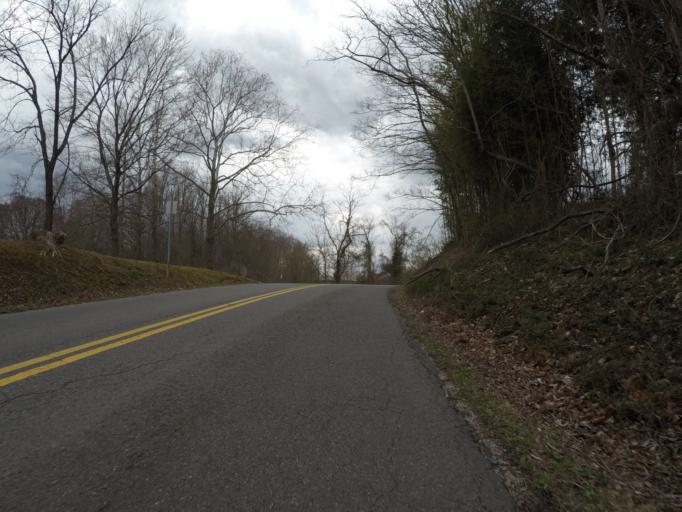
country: US
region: Ohio
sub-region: Lawrence County
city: Burlington
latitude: 38.4329
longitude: -82.5286
